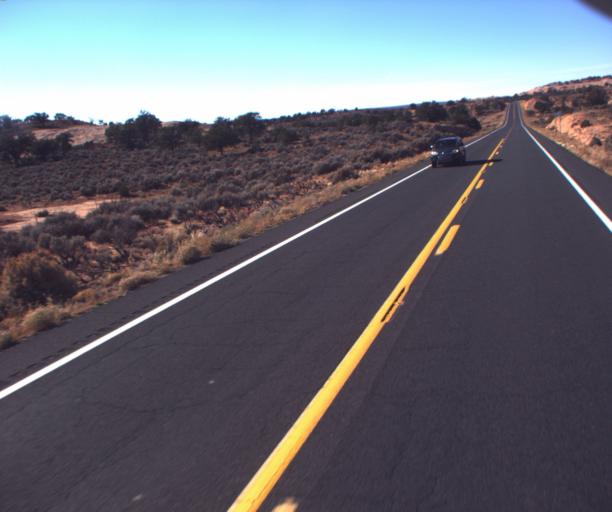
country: US
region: Arizona
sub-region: Coconino County
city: Kaibito
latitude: 36.5572
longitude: -110.7142
